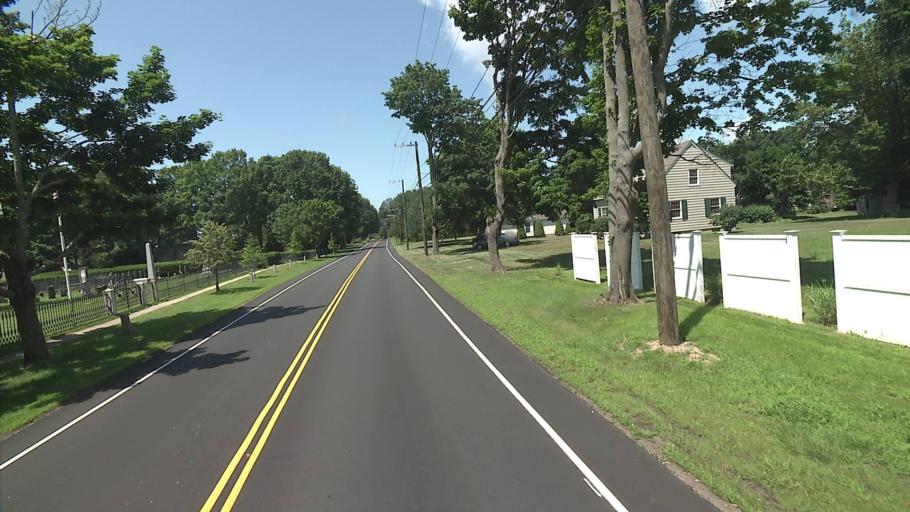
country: US
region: Connecticut
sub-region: Middlesex County
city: Old Saybrook Center
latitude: 41.2839
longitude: -72.3547
